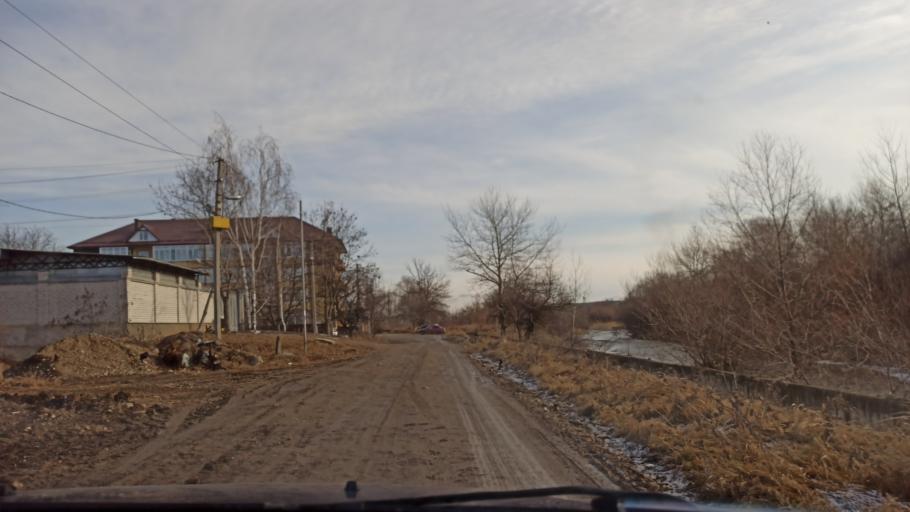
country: RU
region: Stavropol'skiy
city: Yessentukskaya
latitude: 44.0381
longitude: 42.8835
